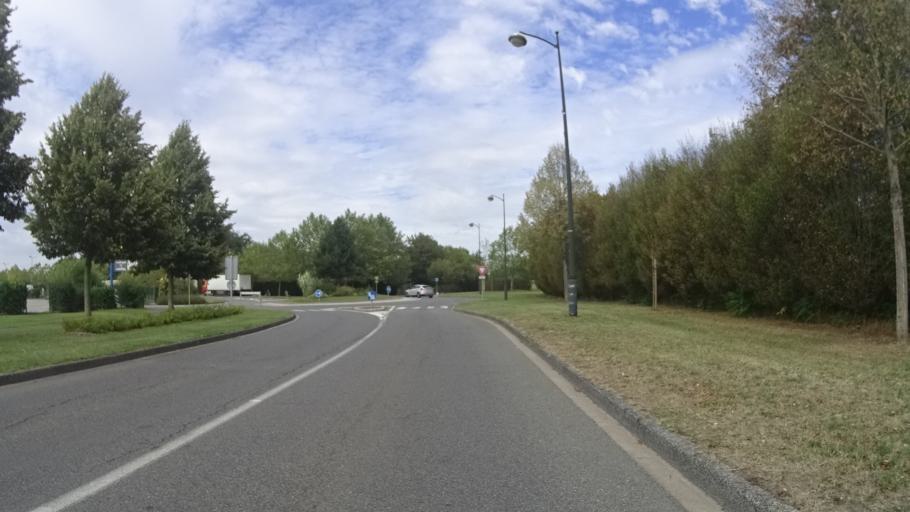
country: FR
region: Centre
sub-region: Departement du Loiret
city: Briare
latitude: 47.6560
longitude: 2.7373
